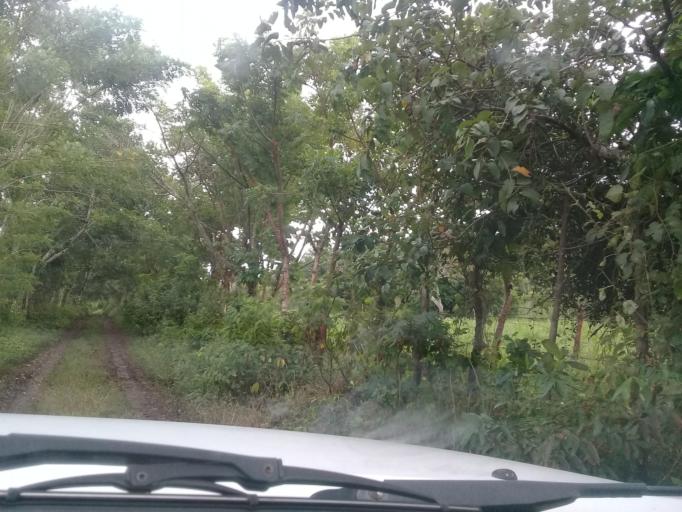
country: MX
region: Veracruz
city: Santiago Tuxtla
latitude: 18.4645
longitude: -95.2842
